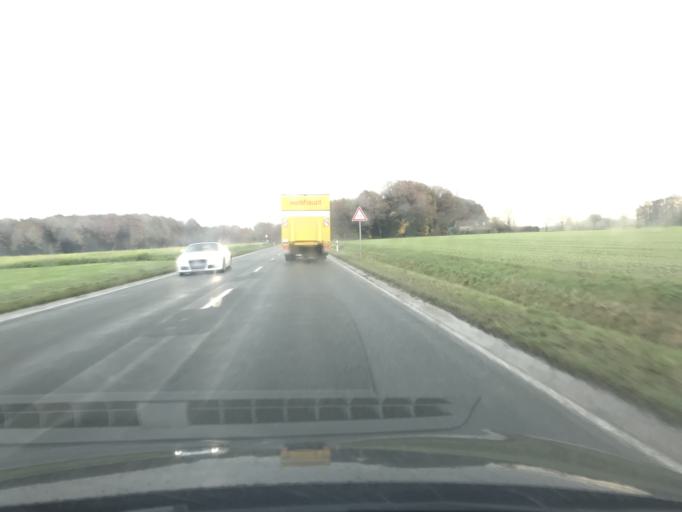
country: DE
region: North Rhine-Westphalia
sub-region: Regierungsbezirk Munster
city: Everswinkel
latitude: 51.9287
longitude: 7.8812
